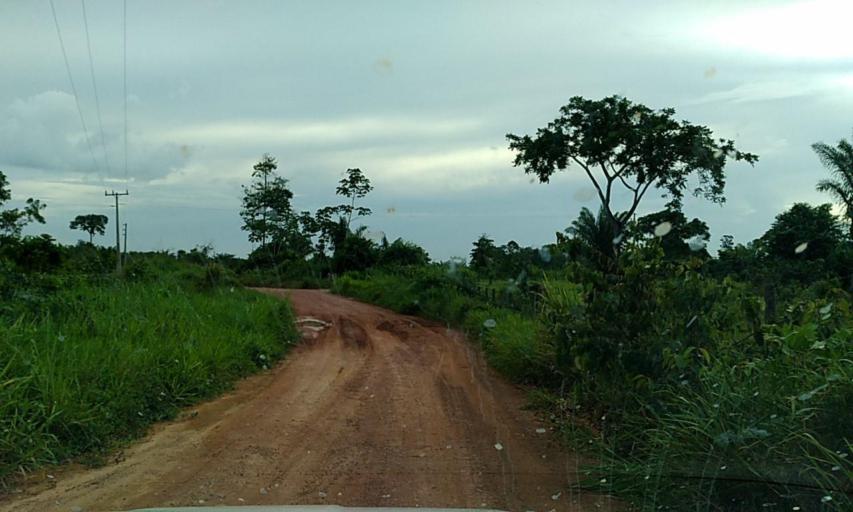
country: BR
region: Para
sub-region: Senador Jose Porfirio
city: Senador Jose Porfirio
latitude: -2.5500
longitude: -51.8642
